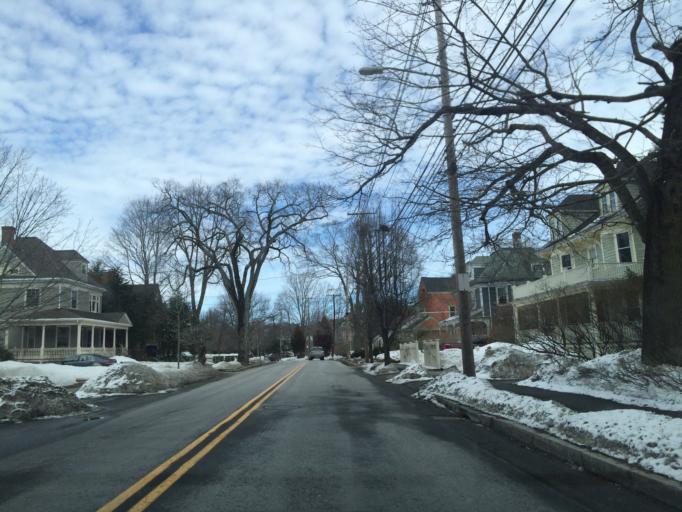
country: US
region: Massachusetts
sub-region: Middlesex County
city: Lexington
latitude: 42.4434
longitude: -71.2298
